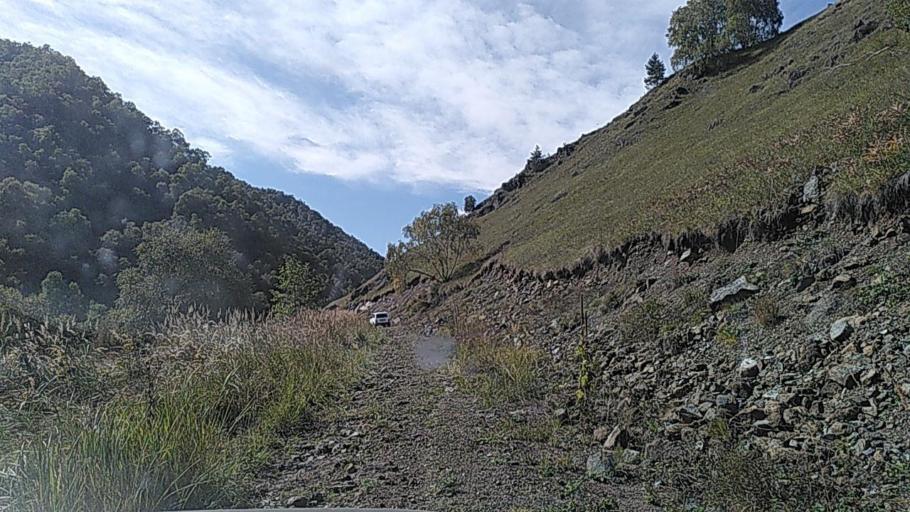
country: RU
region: Kabardino-Balkariya
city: Kamennomostskoye
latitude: 43.6959
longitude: 42.8384
